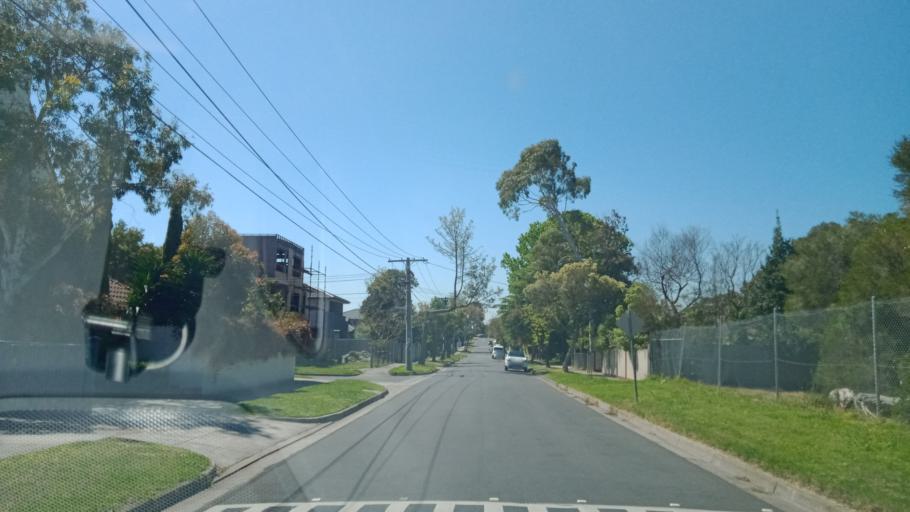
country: AU
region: Victoria
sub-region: Monash
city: Oakleigh South
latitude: -37.9273
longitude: 145.0857
